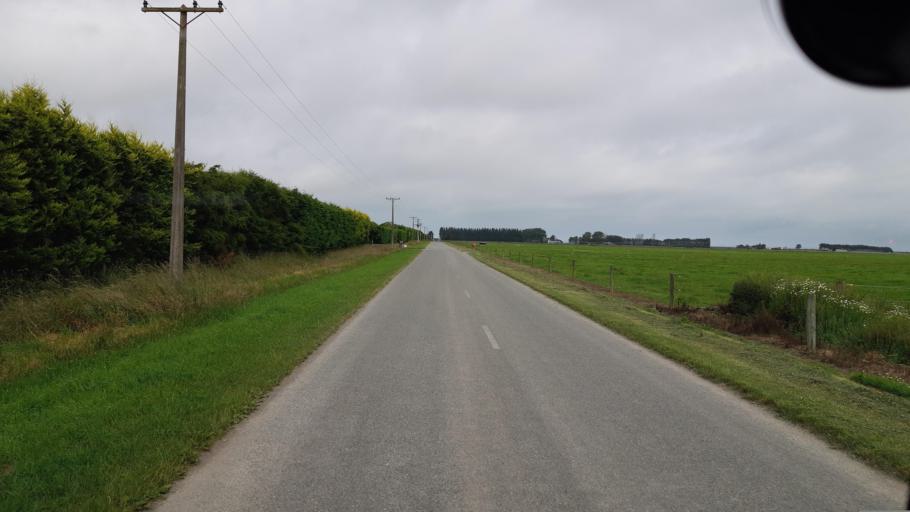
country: NZ
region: Canterbury
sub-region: Timaru District
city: Timaru
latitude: -44.2498
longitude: 171.3522
